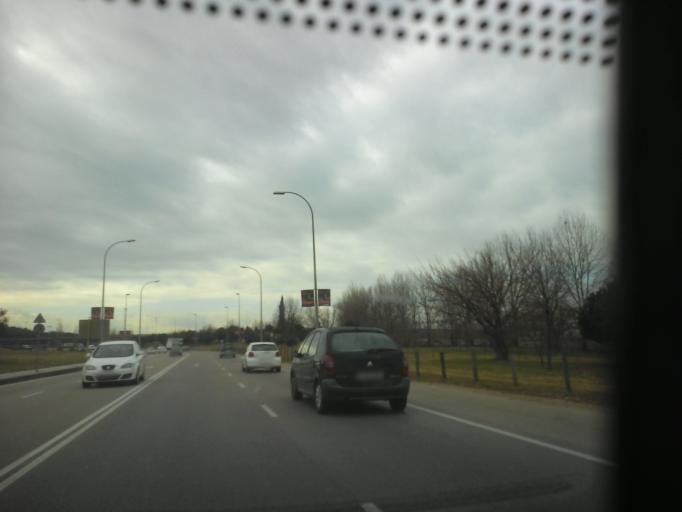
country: ES
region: Catalonia
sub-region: Provincia de Girona
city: Salt
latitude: 41.9598
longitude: 2.8103
